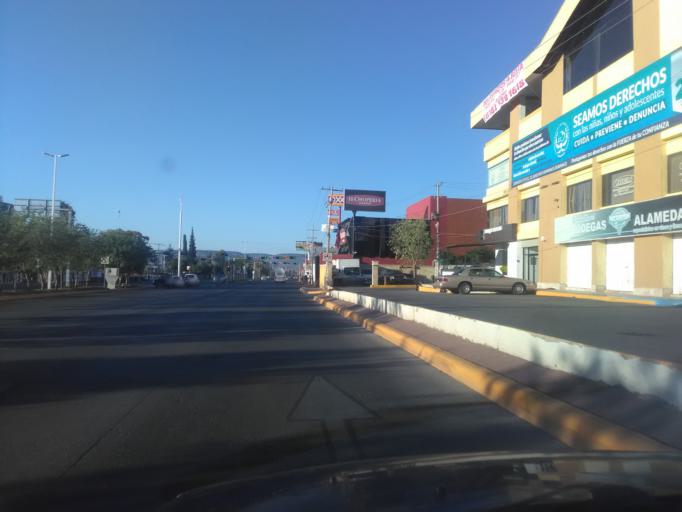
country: MX
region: Durango
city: Victoria de Durango
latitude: 24.0172
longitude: -104.6902
